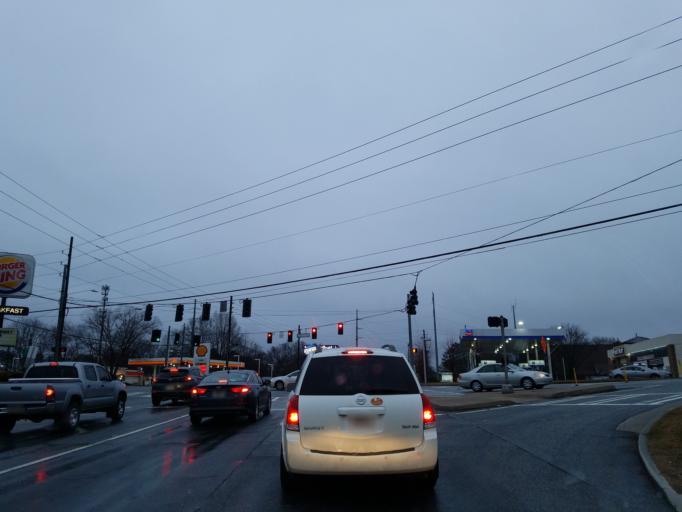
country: US
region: Georgia
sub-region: Gwinnett County
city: Norcross
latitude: 33.9680
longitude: -84.2577
